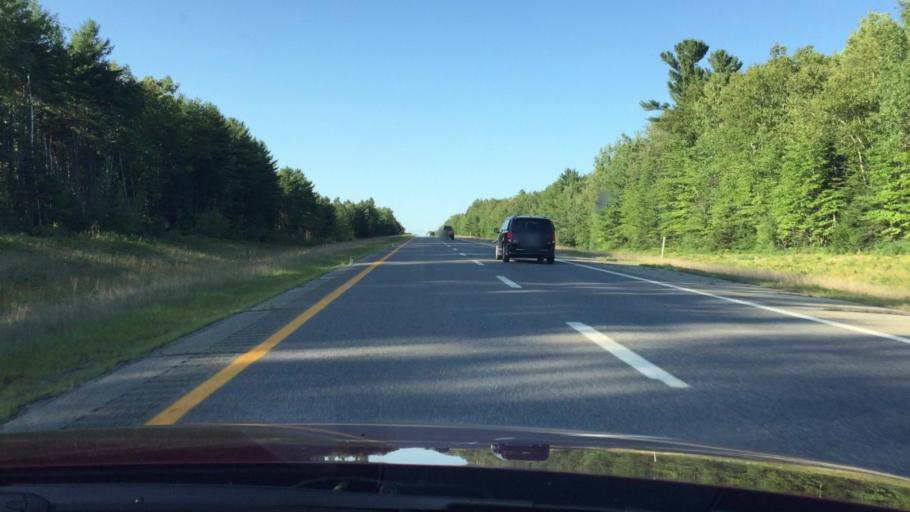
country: US
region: Maine
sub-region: Penobscot County
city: Lincoln
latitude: 45.4095
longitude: -68.5948
